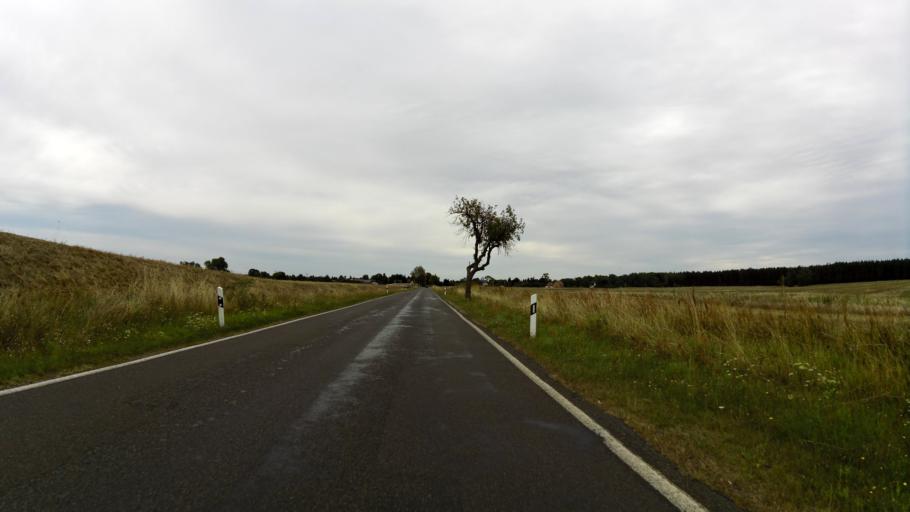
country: DE
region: Brandenburg
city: Wendisch Rietz
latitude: 52.1907
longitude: 14.0402
